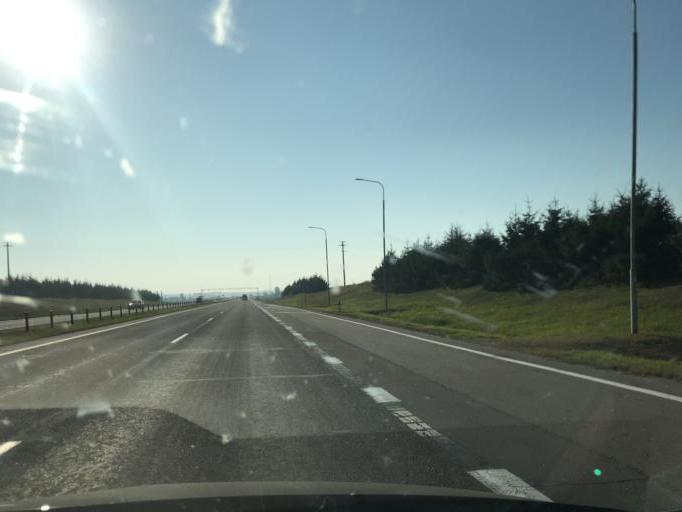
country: BY
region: Minsk
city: Haradzyeya
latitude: 53.3548
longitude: 26.4654
